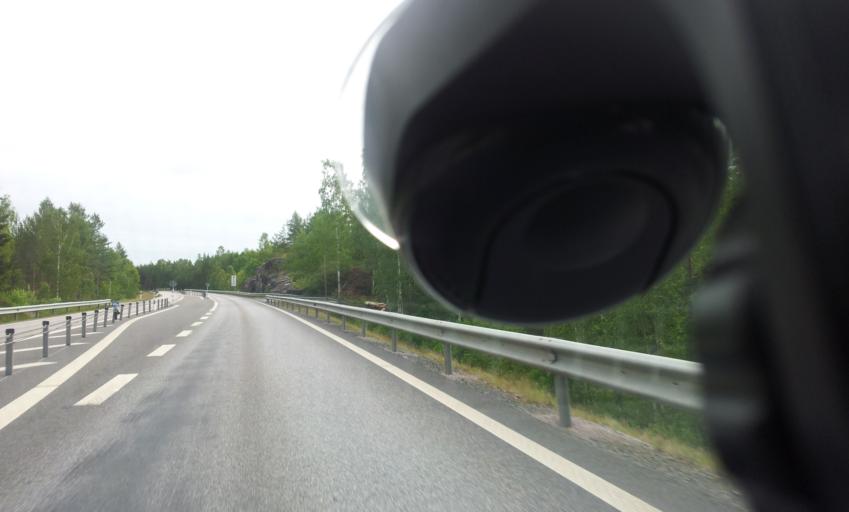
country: SE
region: OEstergoetland
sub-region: Valdemarsviks Kommun
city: Valdemarsvik
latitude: 58.0987
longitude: 16.5353
